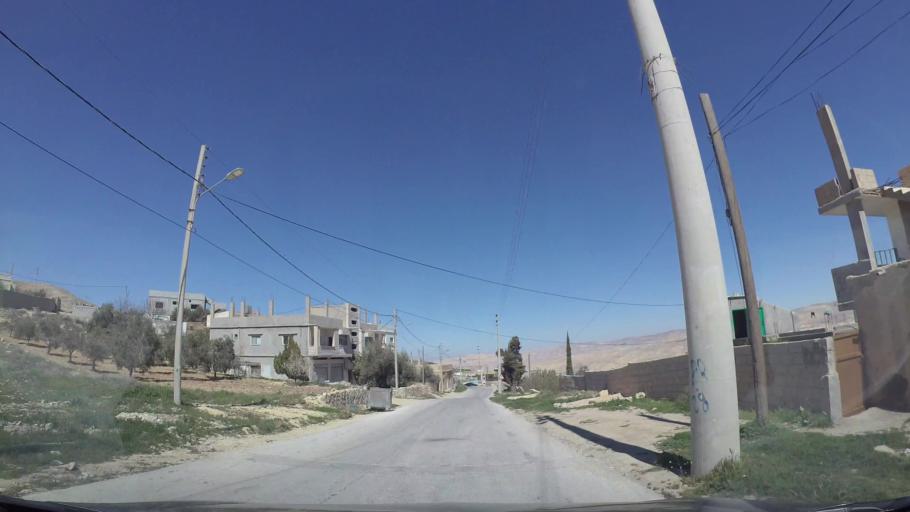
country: JO
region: Tafielah
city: At Tafilah
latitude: 30.8288
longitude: 35.5796
